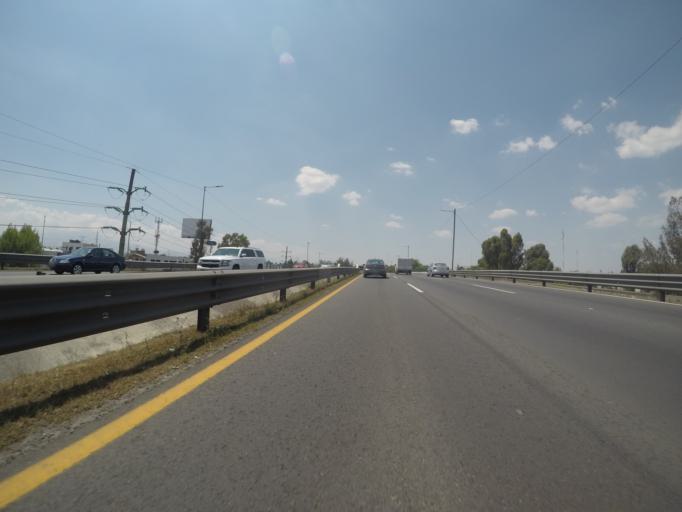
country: MX
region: Mexico
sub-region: Lerma
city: Colonia Isidro Fabela
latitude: 19.2852
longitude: -99.5283
